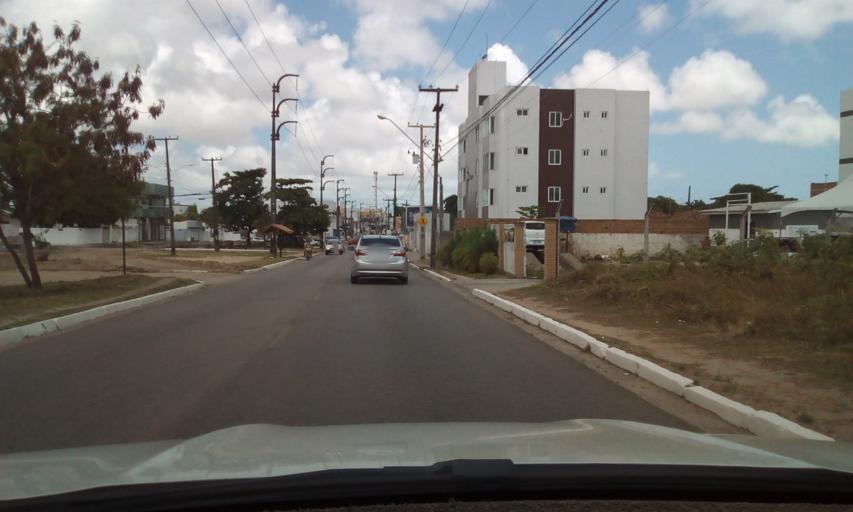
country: BR
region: Paraiba
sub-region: Joao Pessoa
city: Joao Pessoa
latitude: -7.1789
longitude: -34.8646
